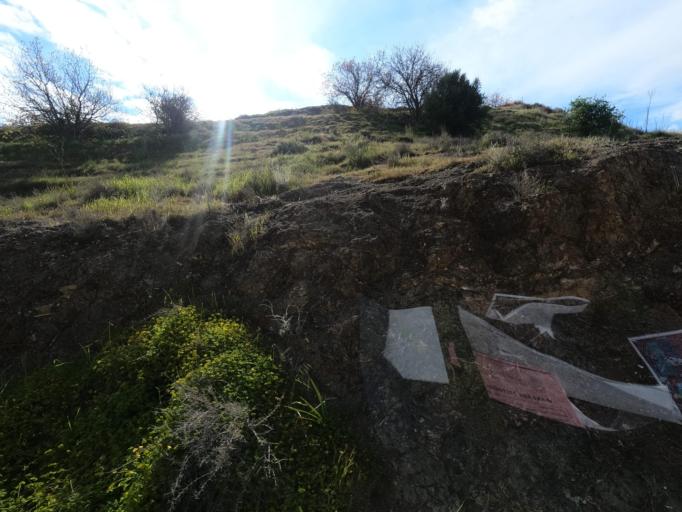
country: CY
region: Lefkosia
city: Lefka
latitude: 35.1055
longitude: 32.8882
